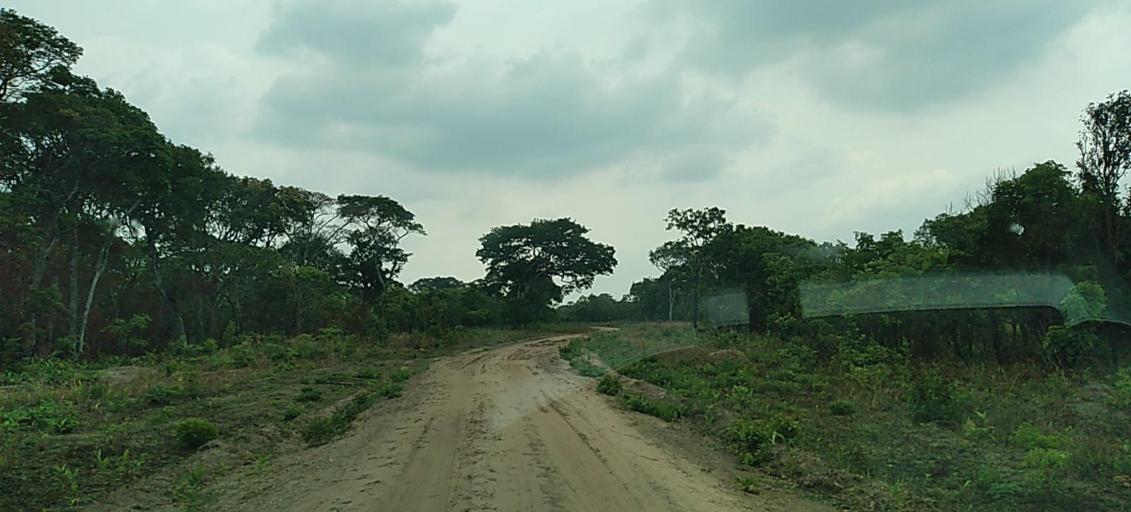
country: ZM
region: North-Western
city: Mwinilunga
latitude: -11.4145
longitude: 24.6098
